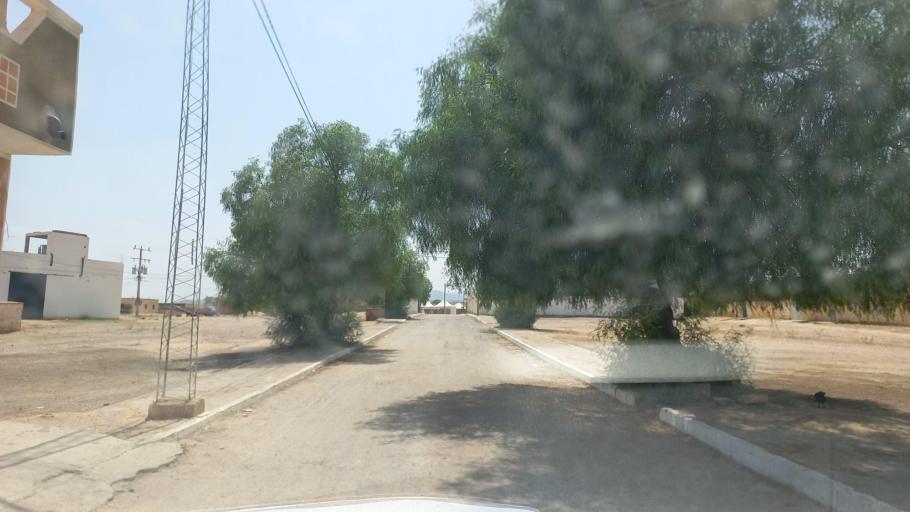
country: TN
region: Al Qasrayn
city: Kasserine
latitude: 35.2525
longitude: 9.0260
